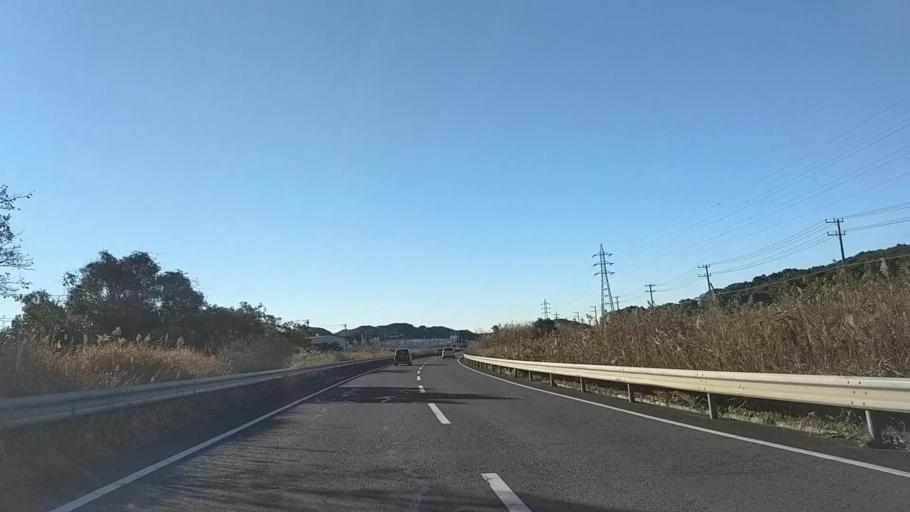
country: JP
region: Chiba
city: Kisarazu
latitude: 35.3661
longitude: 139.9119
